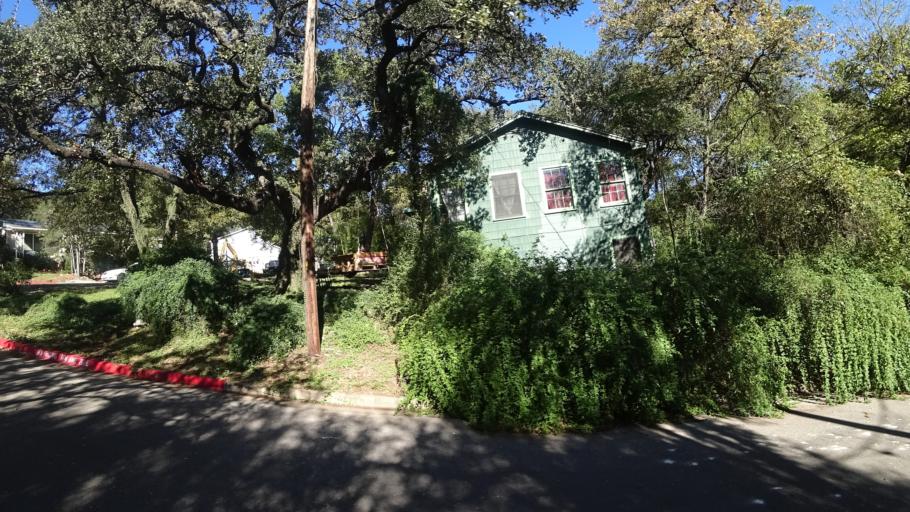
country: US
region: Texas
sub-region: Travis County
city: Rollingwood
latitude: 30.2820
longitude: -97.7700
